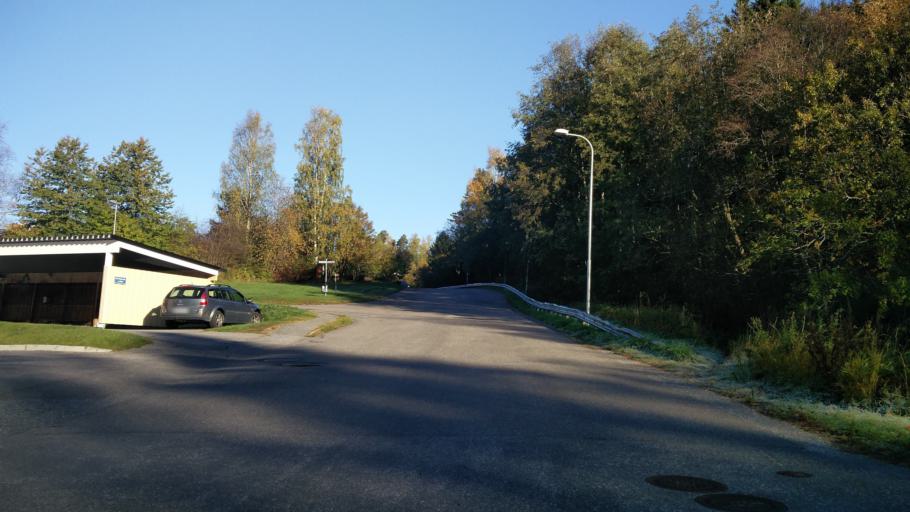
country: SE
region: Vaesternorrland
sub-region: Sundsvalls Kommun
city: Sundsvall
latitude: 62.4045
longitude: 17.2657
